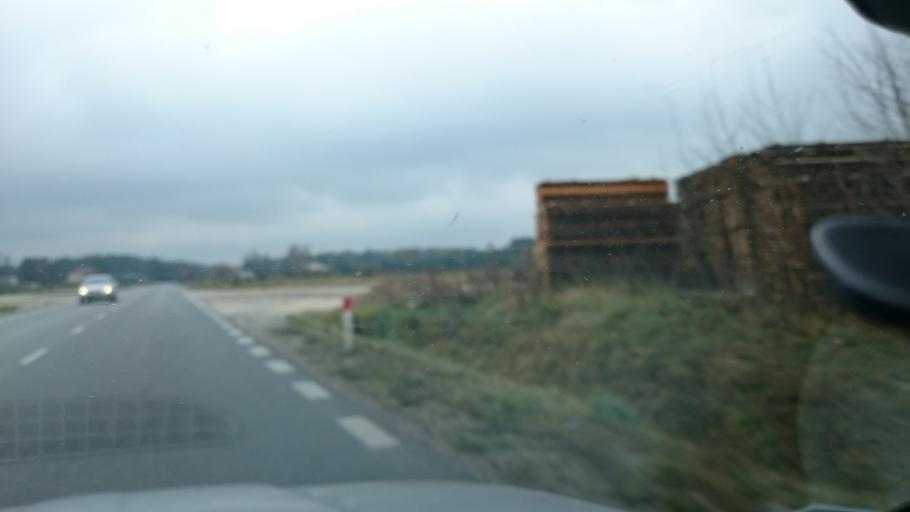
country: PL
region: Swietokrzyskie
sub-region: Powiat konecki
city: Konskie
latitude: 51.1321
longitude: 20.3614
